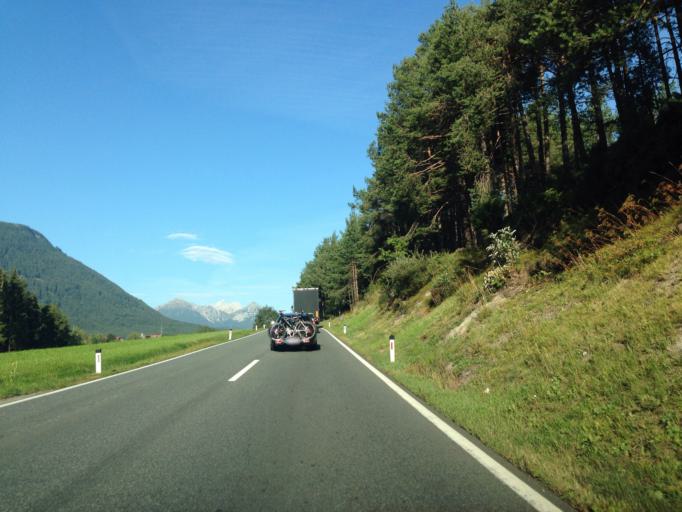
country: AT
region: Tyrol
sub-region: Politischer Bezirk Imst
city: Obsteig
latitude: 47.2986
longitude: 10.9387
